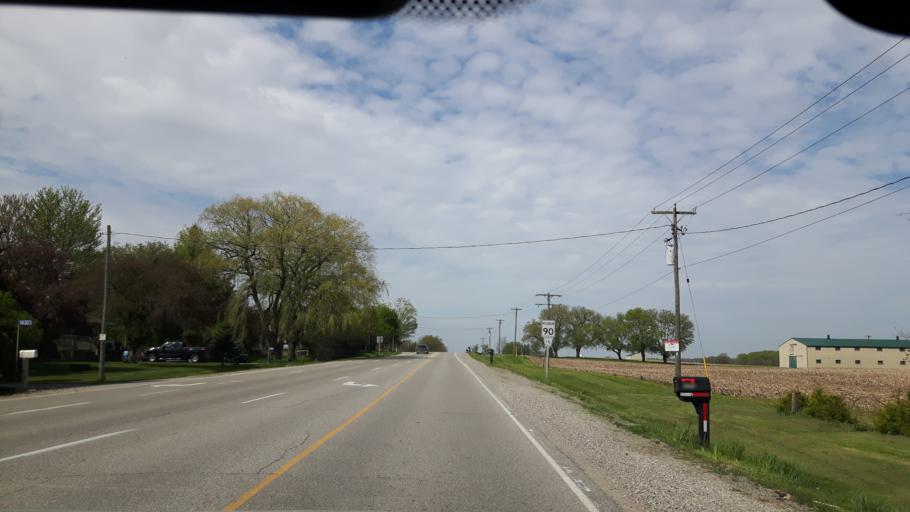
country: CA
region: Ontario
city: London
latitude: 43.0973
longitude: -81.3198
